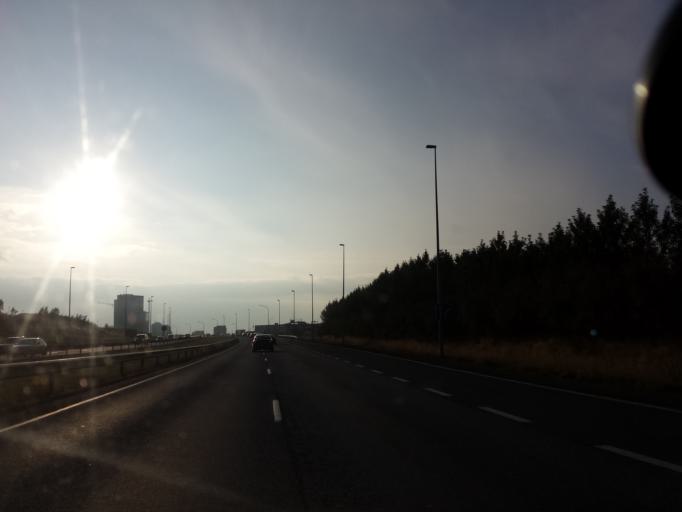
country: IS
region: Capital Region
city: Reykjavik
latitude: 64.1054
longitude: -21.8602
